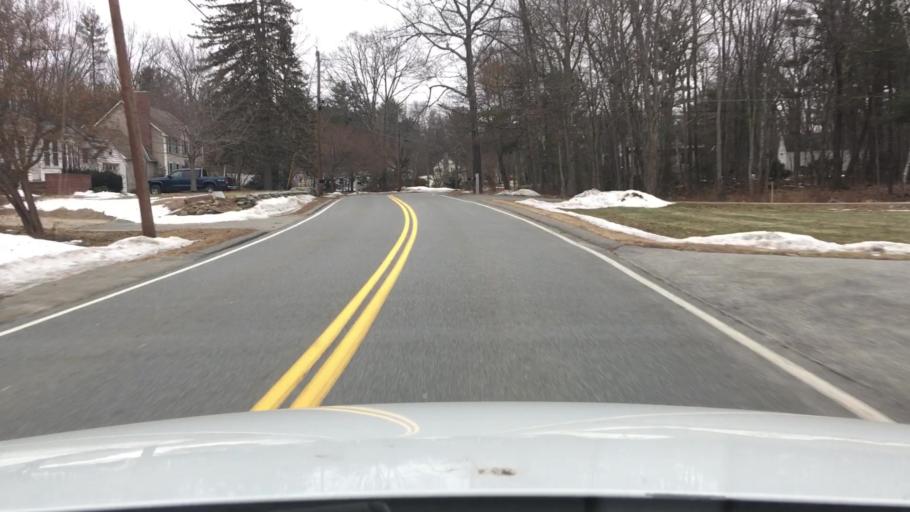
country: US
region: New Hampshire
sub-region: Rockingham County
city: Salem
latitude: 42.7980
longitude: -71.2284
